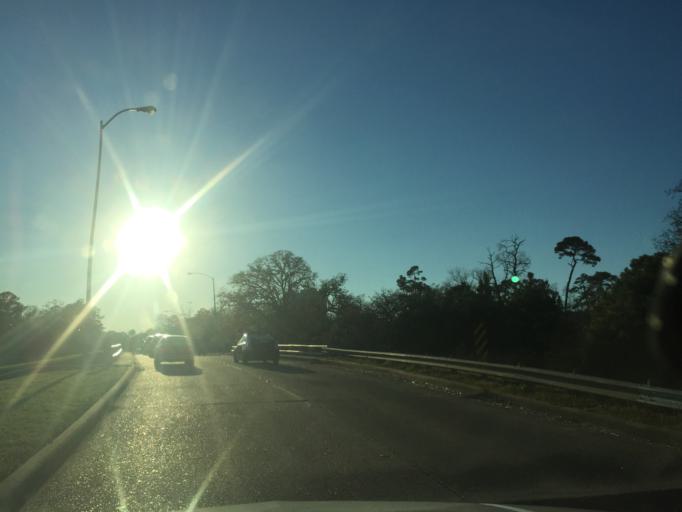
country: US
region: Texas
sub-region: Harris County
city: Hunters Creek Village
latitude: 29.7687
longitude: -95.4498
